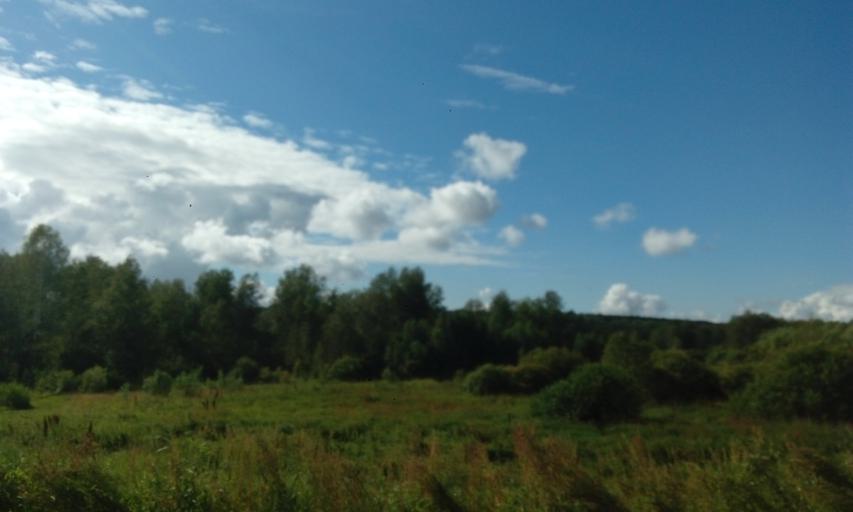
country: RU
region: Novosibirsk
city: Iskitim
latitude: 54.7707
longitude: 83.2686
